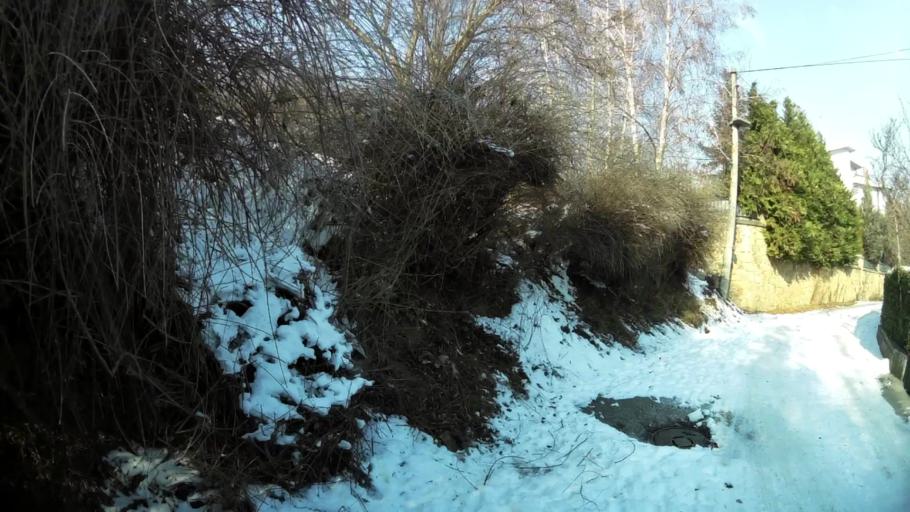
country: MK
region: Karpos
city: Skopje
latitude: 41.9802
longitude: 21.4264
